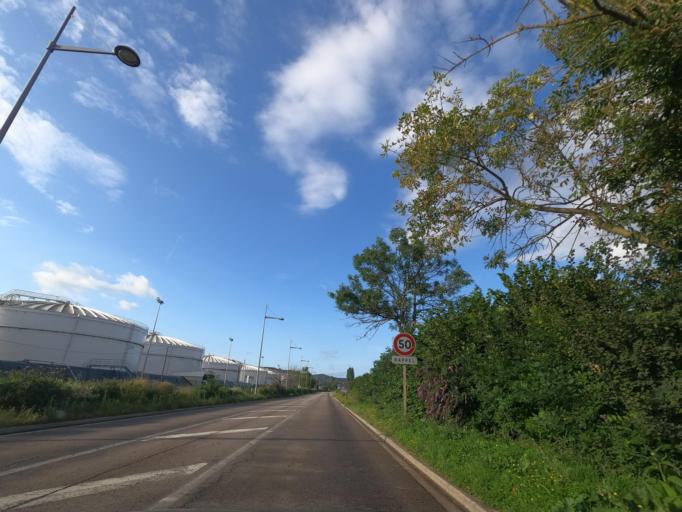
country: FR
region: Haute-Normandie
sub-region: Departement de la Seine-Maritime
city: Petit-Couronne
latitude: 49.4042
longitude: 1.0158
